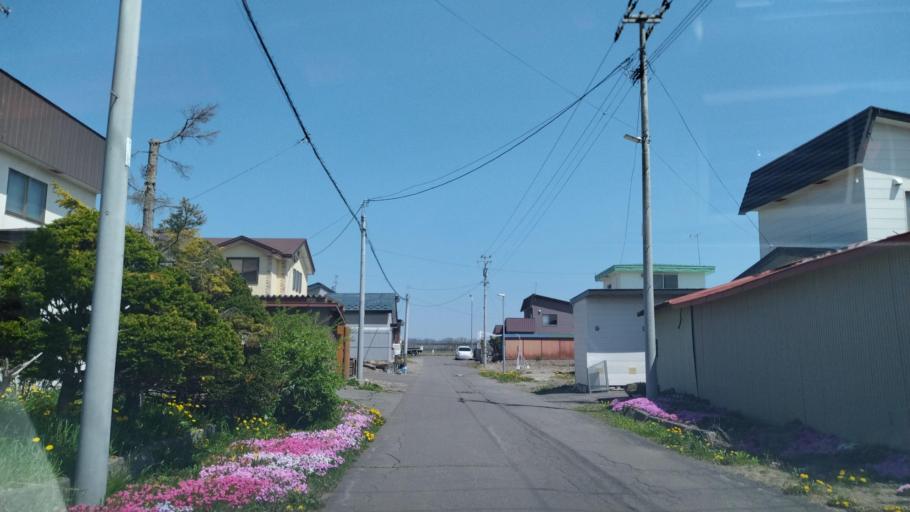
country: JP
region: Hokkaido
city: Otofuke
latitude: 43.2398
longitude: 143.2907
